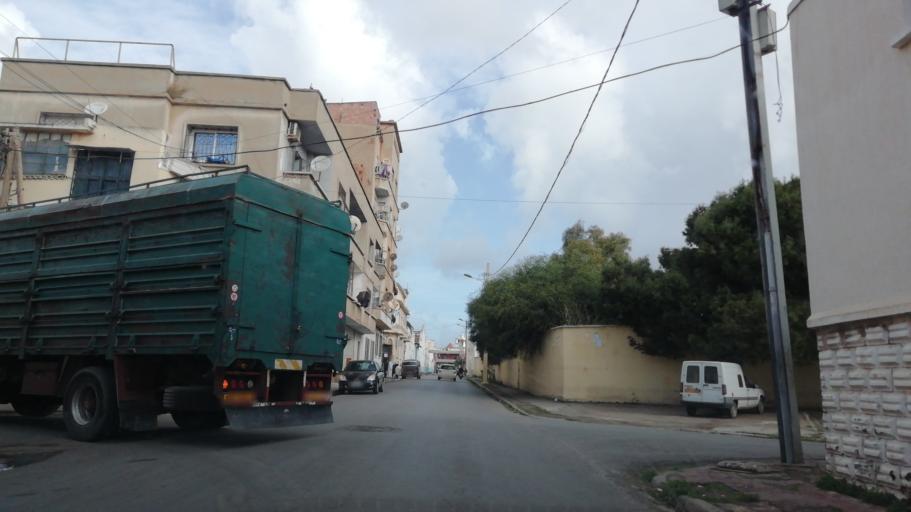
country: DZ
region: Oran
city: Oran
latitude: 35.6907
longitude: -0.6311
